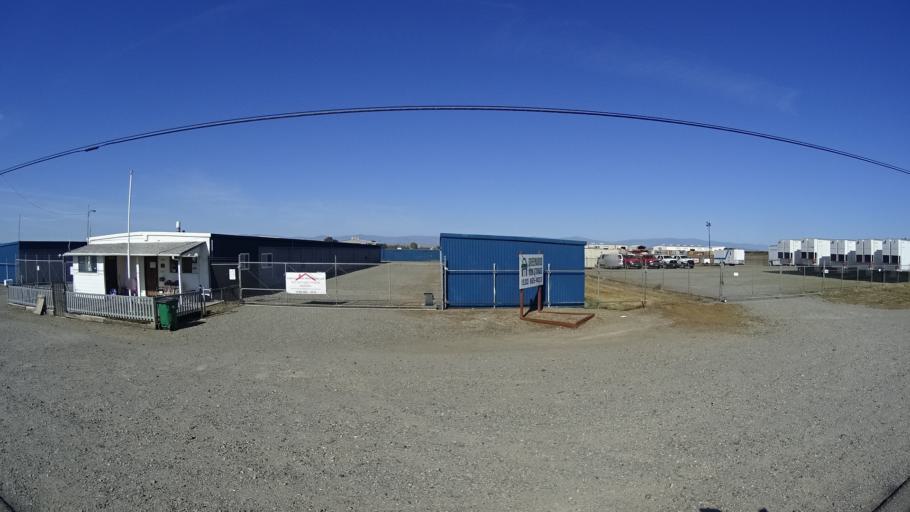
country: US
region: California
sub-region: Glenn County
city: Orland
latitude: 39.6836
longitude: -122.1969
